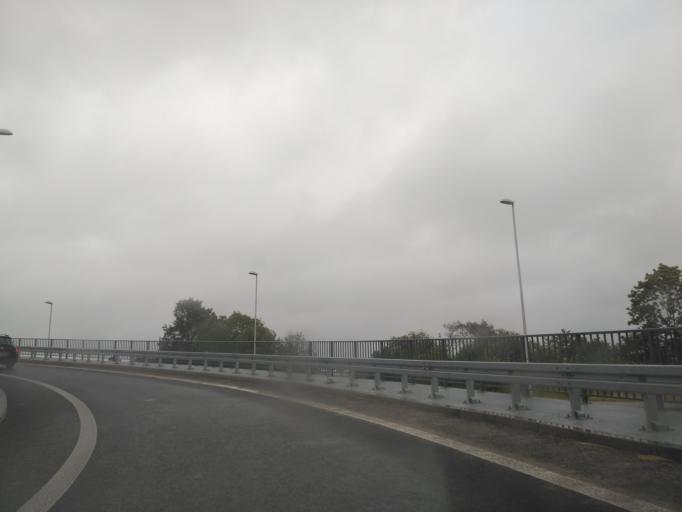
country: PL
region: Lublin Voivodeship
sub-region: Powiat lubelski
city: Lublin
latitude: 51.2829
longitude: 22.5768
